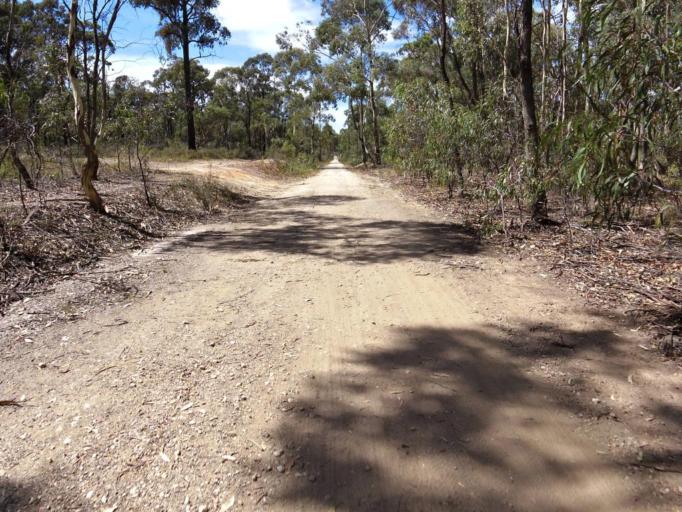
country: AU
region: Victoria
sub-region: Greater Bendigo
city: White Hills
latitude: -36.7584
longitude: 144.3327
